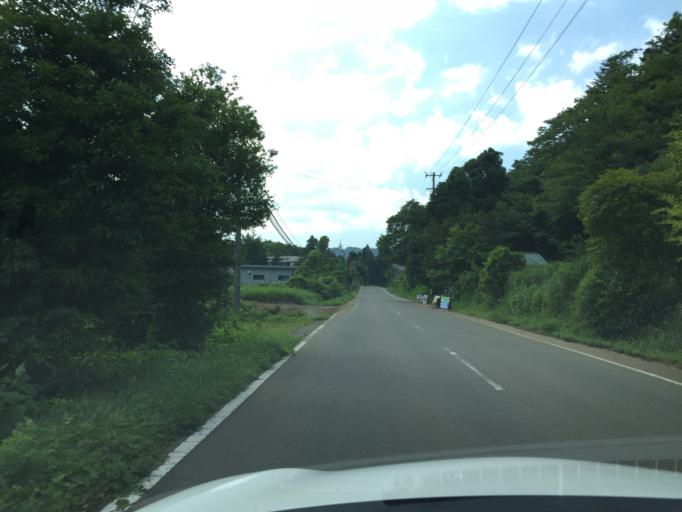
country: JP
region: Fukushima
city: Iwaki
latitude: 37.0561
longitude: 140.6923
